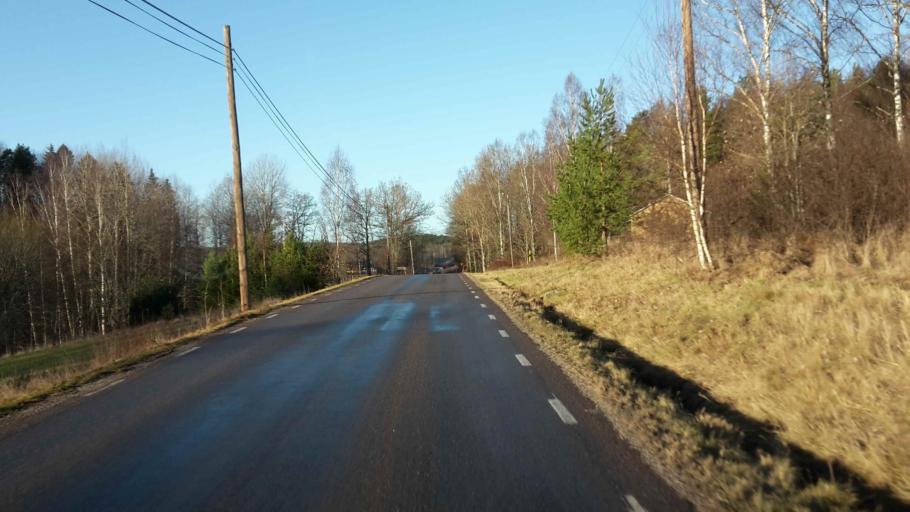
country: SE
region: Kalmar
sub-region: Vasterviks Kommun
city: Overum
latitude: 58.1489
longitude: 16.3192
